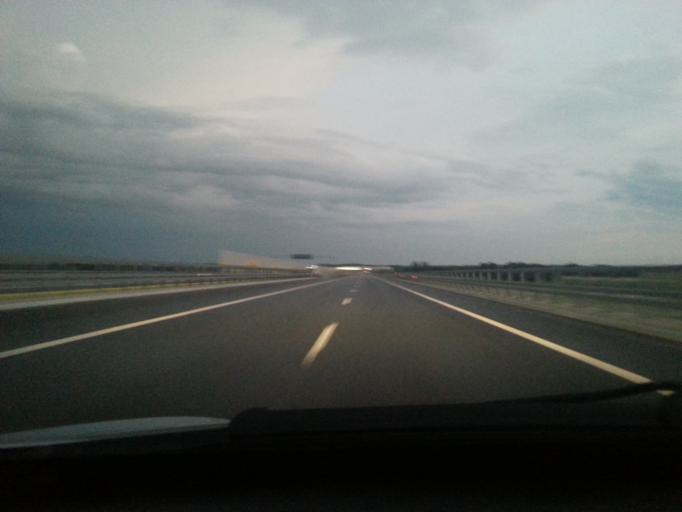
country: PL
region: Lodz Voivodeship
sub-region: Powiat sieradzki
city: Sieradz
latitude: 51.5819
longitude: 18.7996
